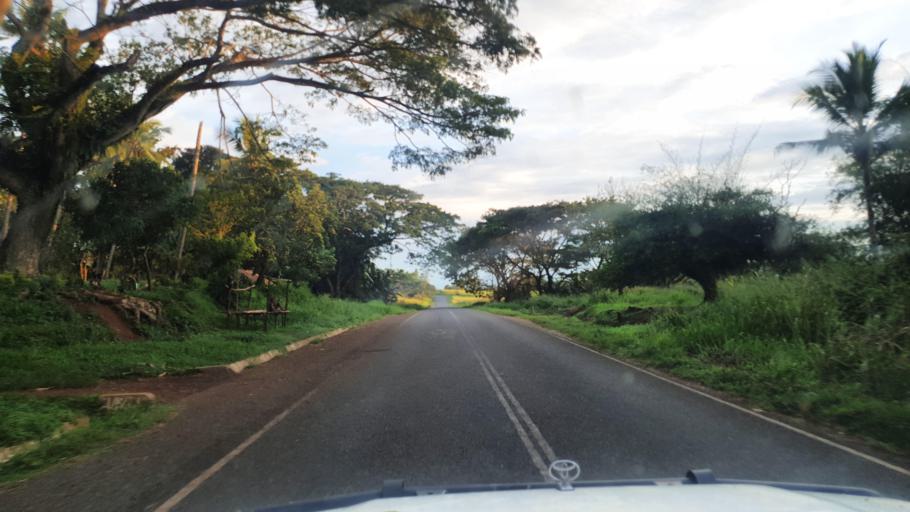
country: PG
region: National Capital
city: Port Moresby
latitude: -9.0812
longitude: 147.1239
